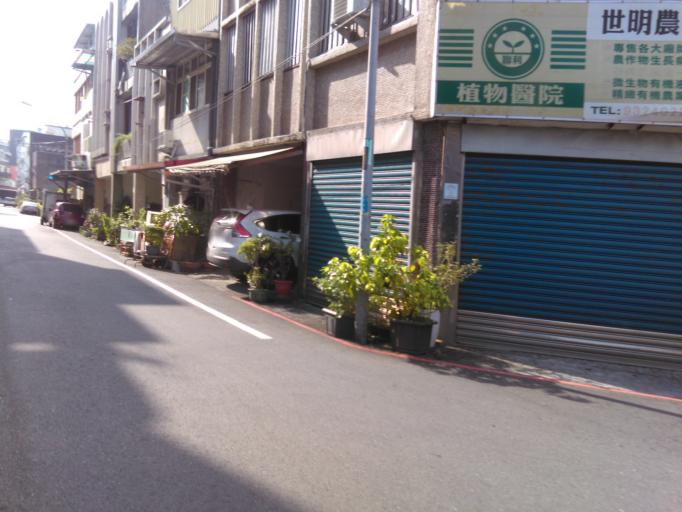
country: TW
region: Taiwan
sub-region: Yilan
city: Yilan
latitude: 24.7521
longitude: 121.7504
